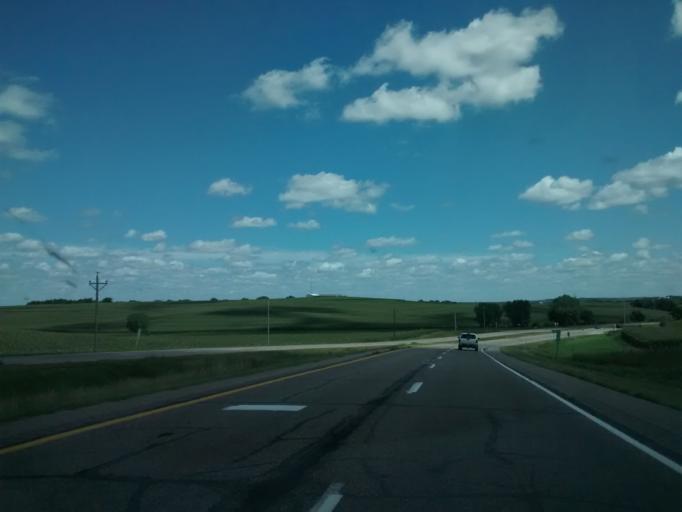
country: US
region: Iowa
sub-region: Woodbury County
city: Moville
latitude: 42.4797
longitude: -96.0981
